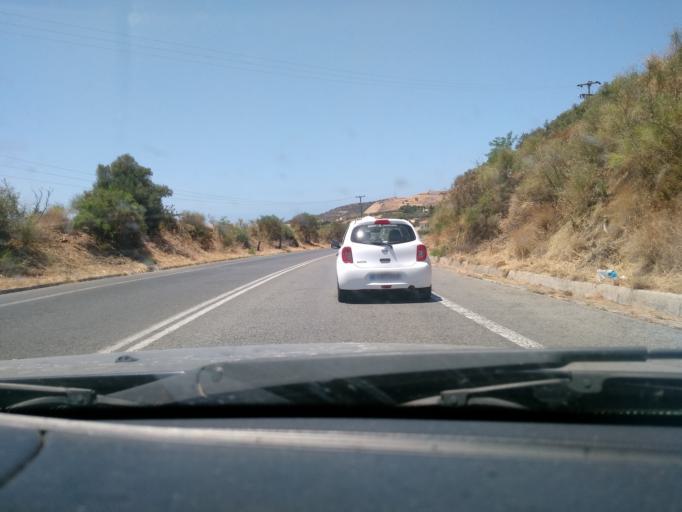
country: GR
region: Crete
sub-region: Nomos Rethymnis
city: Panormos
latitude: 35.4084
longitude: 24.7245
